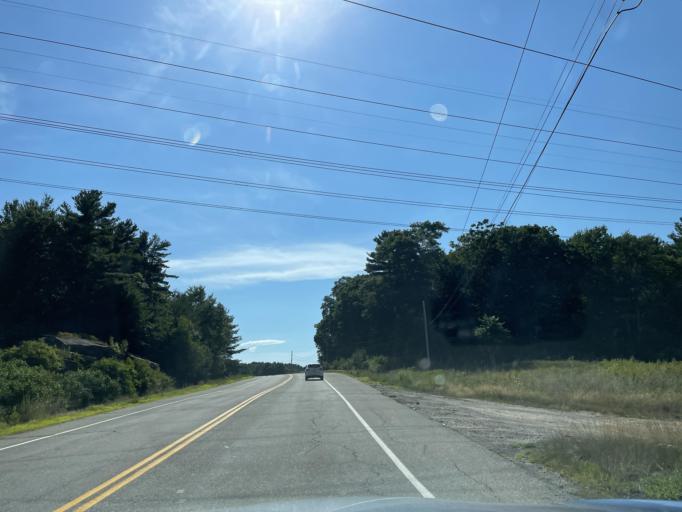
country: US
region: Massachusetts
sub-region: Worcester County
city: Sutton
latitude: 42.1507
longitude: -71.7180
